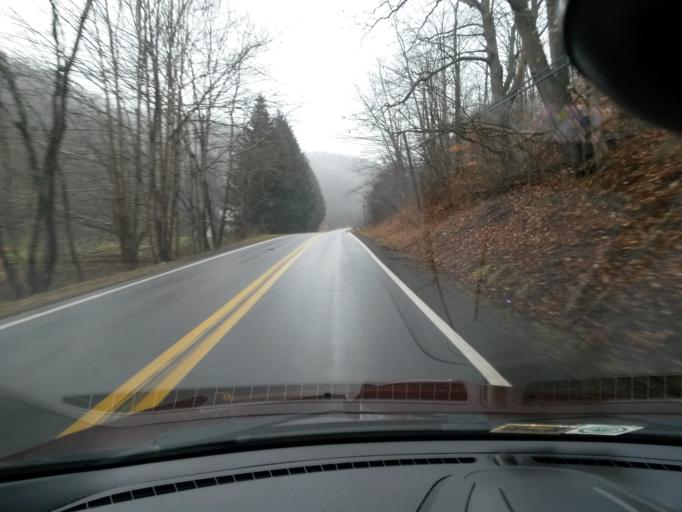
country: US
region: West Virginia
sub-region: Greenbrier County
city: Lewisburg
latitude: 37.8718
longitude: -80.4972
